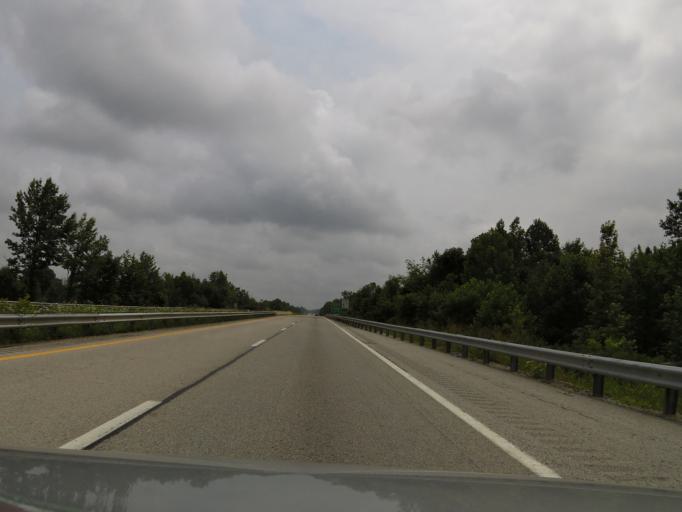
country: US
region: Kentucky
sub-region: Ohio County
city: Beaver Dam
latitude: 37.3556
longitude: -86.8794
